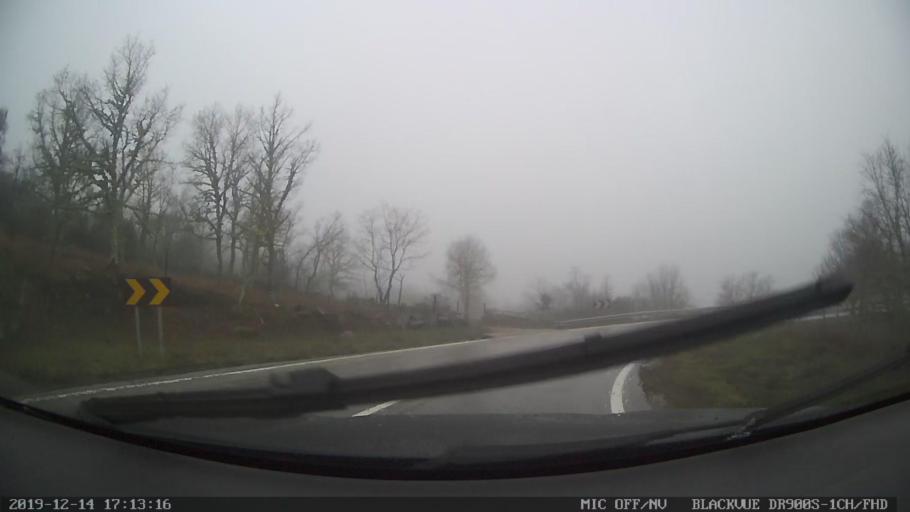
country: PT
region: Vila Real
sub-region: Vila Pouca de Aguiar
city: Vila Pouca de Aguiar
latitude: 41.4954
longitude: -7.6257
